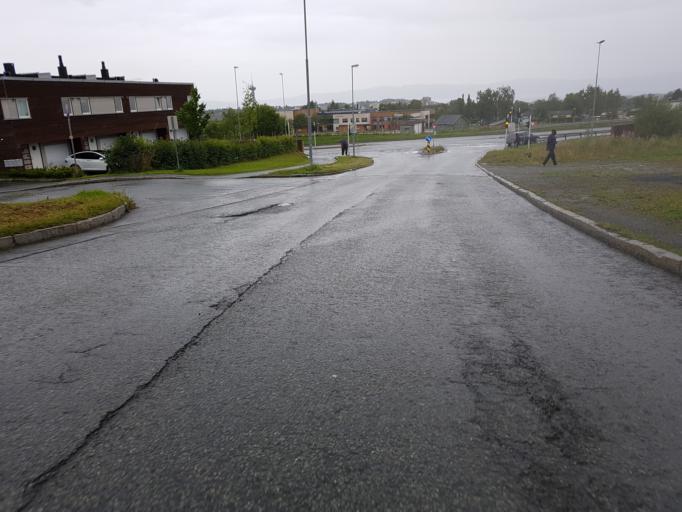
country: NO
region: Sor-Trondelag
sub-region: Trondheim
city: Trondheim
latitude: 63.4095
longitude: 10.4554
